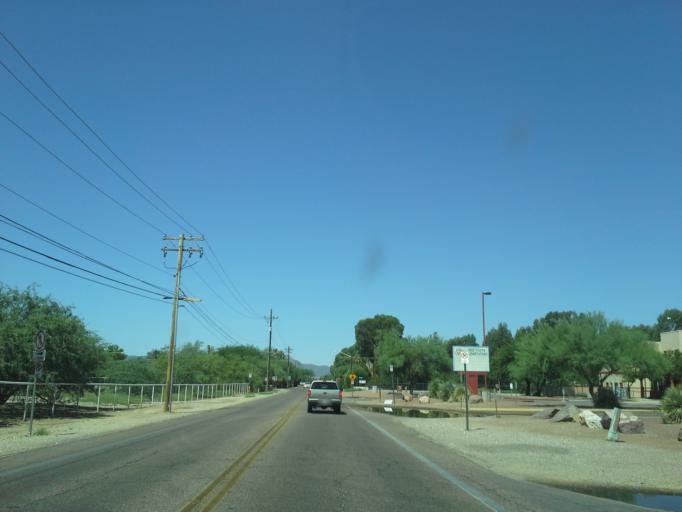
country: US
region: Arizona
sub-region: Pima County
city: Catalina Foothills
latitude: 32.2831
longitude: -110.9507
